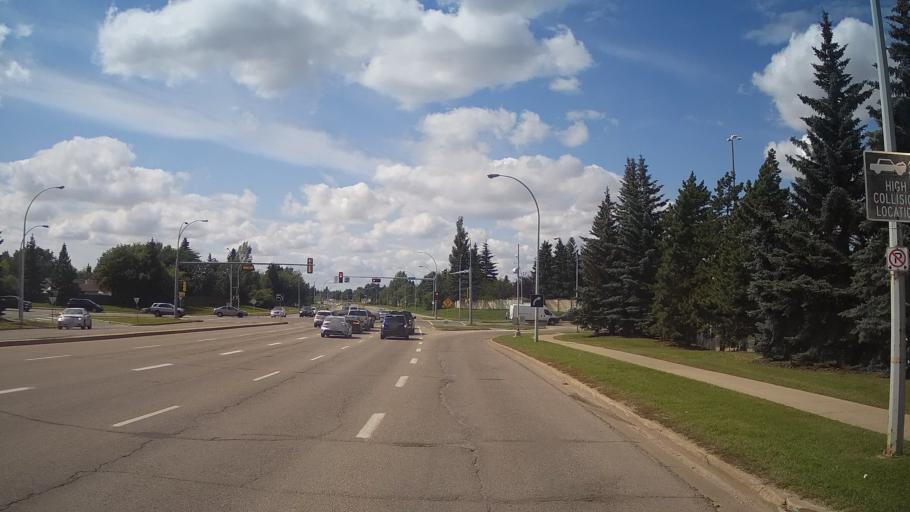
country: CA
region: Alberta
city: St. Albert
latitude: 53.5212
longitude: -113.6289
